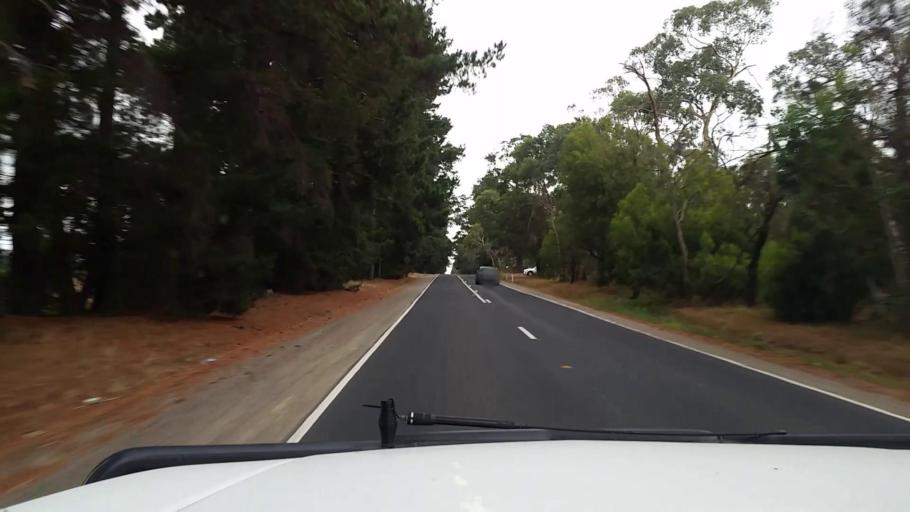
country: AU
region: Victoria
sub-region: Mornington Peninsula
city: Somerville
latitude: -38.2266
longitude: 145.1534
